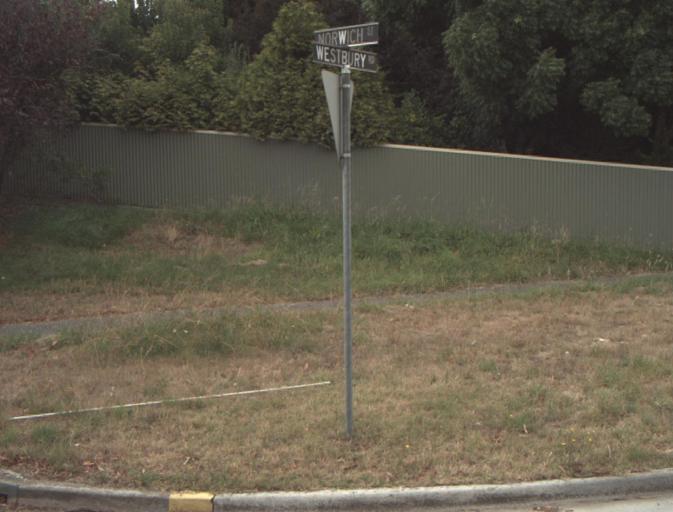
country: AU
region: Tasmania
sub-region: Launceston
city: West Launceston
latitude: -41.4580
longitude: 147.1459
